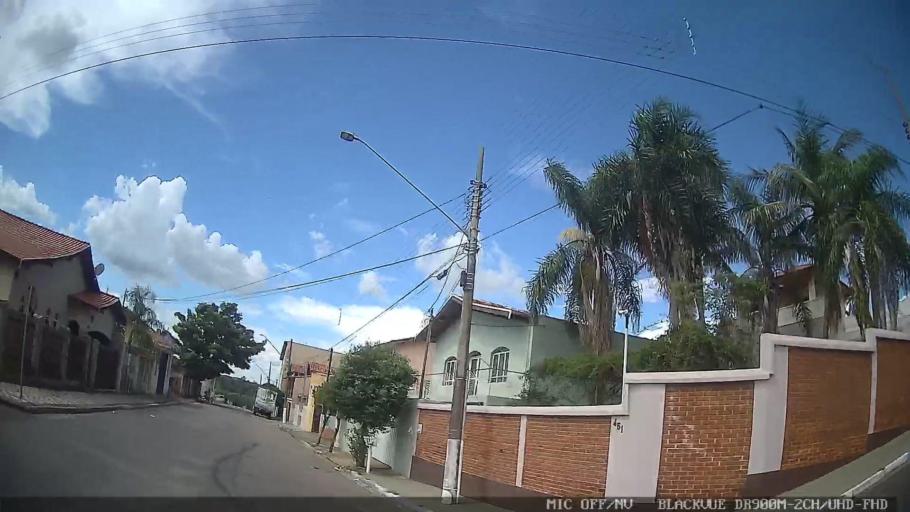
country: BR
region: Sao Paulo
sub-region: Conchas
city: Conchas
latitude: -23.0163
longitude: -48.0119
